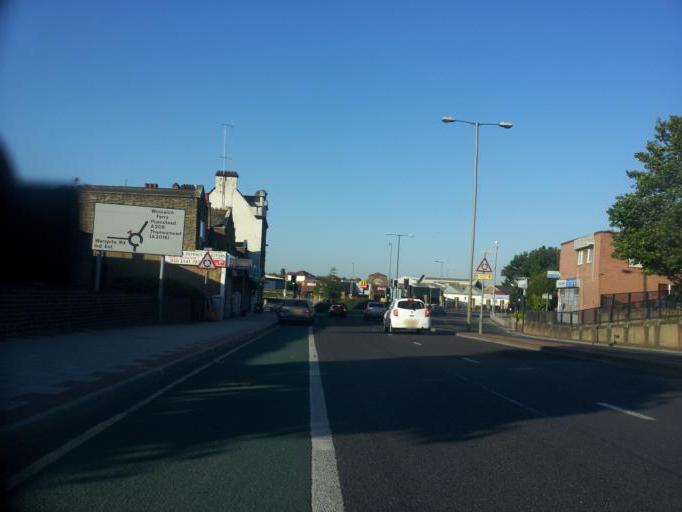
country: GB
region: England
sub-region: Greater London
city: Woolwich
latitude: 51.4923
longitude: 0.0443
